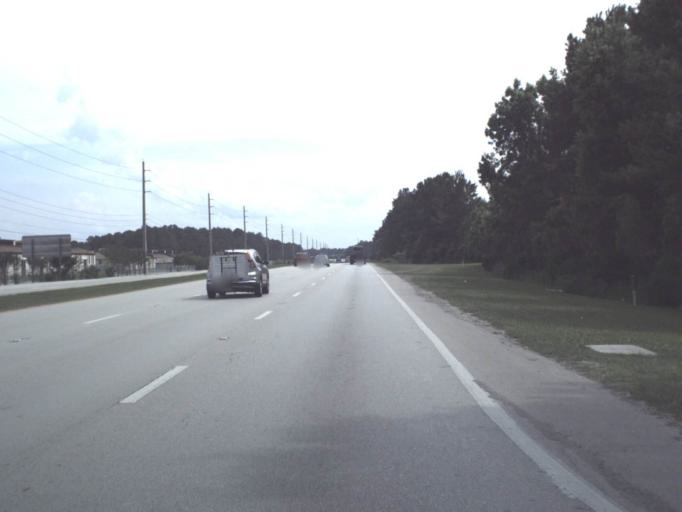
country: US
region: Florida
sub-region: Clay County
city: Orange Park
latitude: 30.2148
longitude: -81.7040
